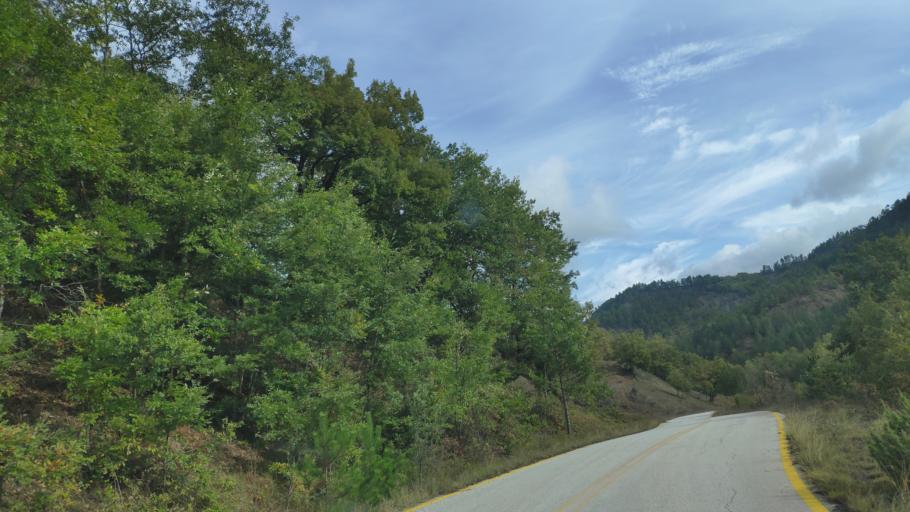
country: GR
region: West Macedonia
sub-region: Nomos Kastorias
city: Nestorio
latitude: 40.2327
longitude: 20.9876
